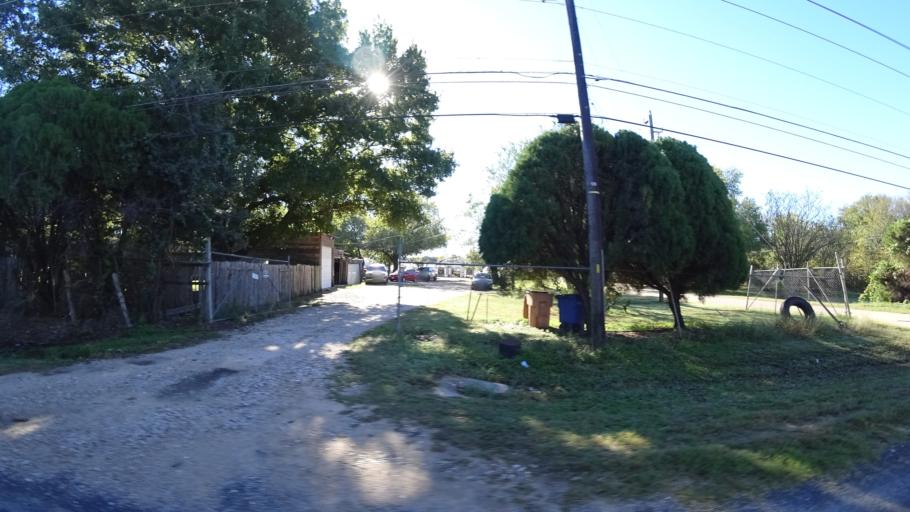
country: US
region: Texas
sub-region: Travis County
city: Austin
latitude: 30.2276
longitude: -97.6735
